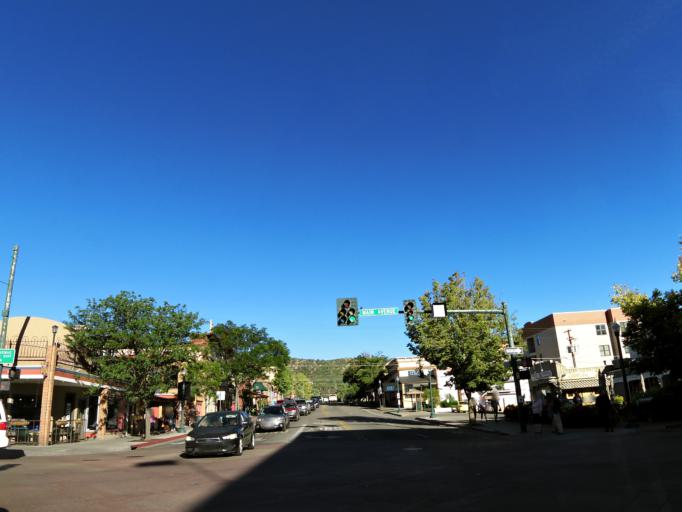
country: US
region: Colorado
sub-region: La Plata County
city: Durango
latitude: 37.2702
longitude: -107.8819
